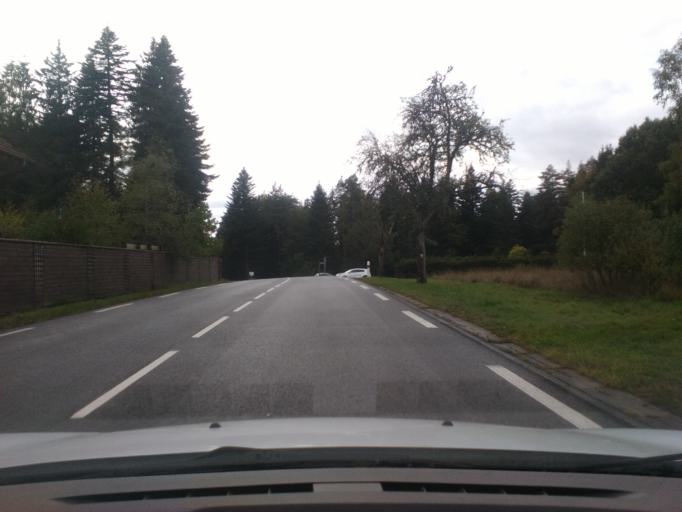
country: FR
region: Lorraine
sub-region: Departement des Vosges
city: Taintrux
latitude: 48.2747
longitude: 6.8634
